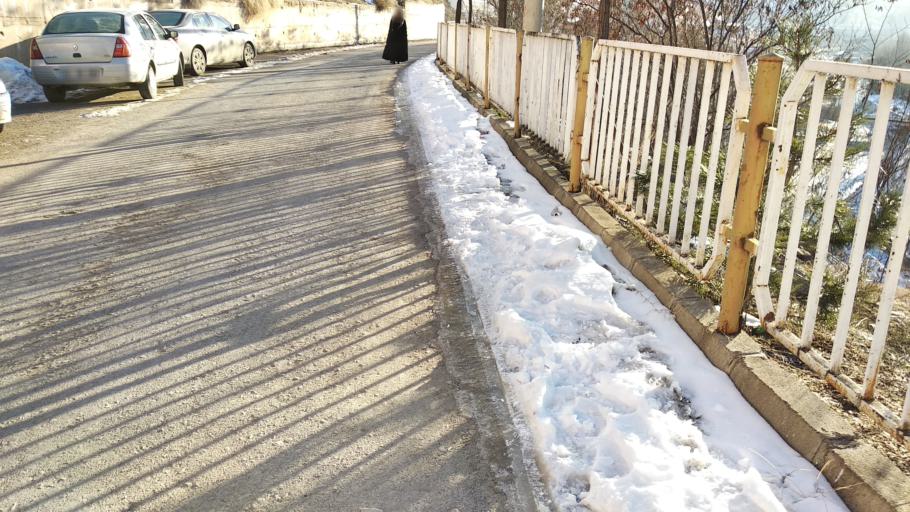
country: TR
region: Gumushane
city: Gumushkhane
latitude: 40.4372
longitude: 39.5101
